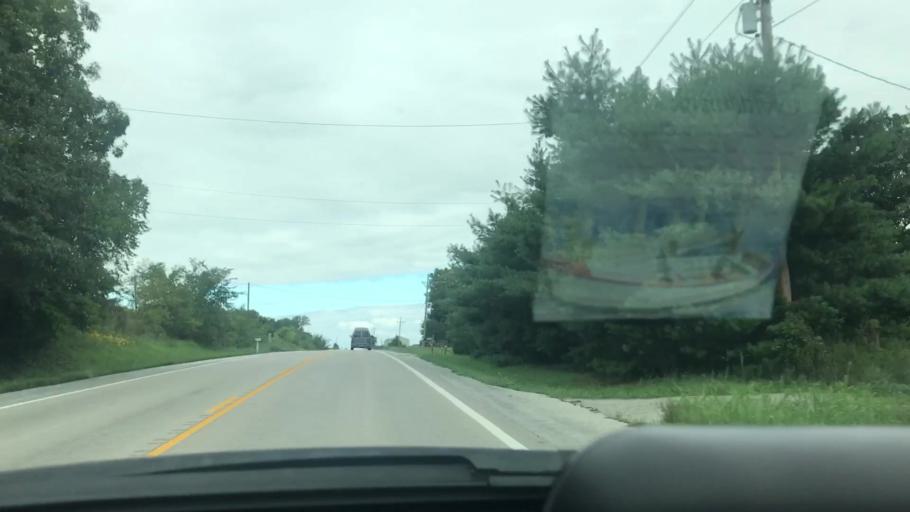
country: US
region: Missouri
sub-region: Hickory County
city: Hermitage
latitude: 37.8789
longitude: -93.1803
